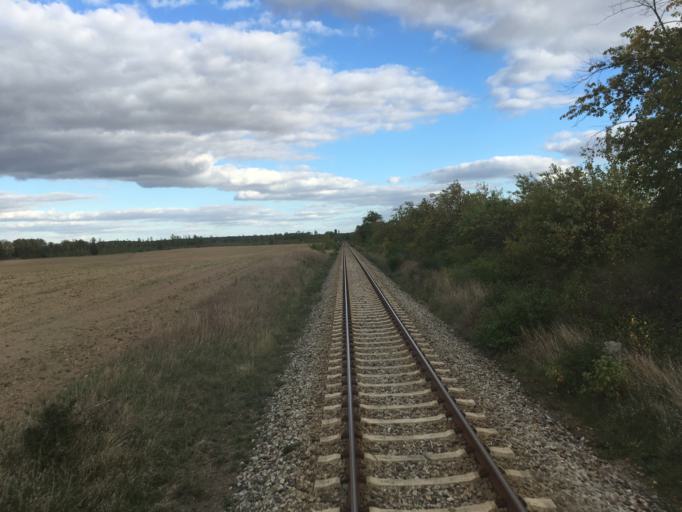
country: DE
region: Mecklenburg-Vorpommern
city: Grabowhofe
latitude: 53.5450
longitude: 12.5612
